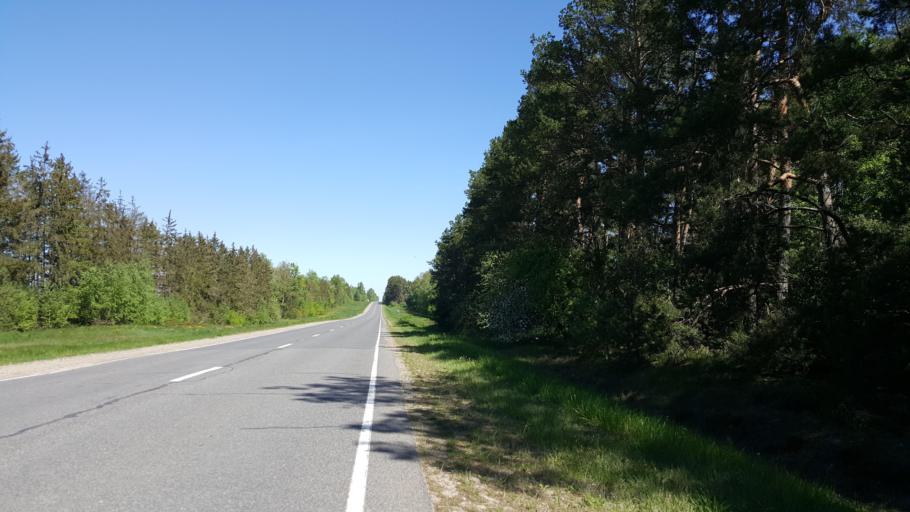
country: BY
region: Brest
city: Kamyanyets
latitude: 52.4517
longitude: 23.7834
